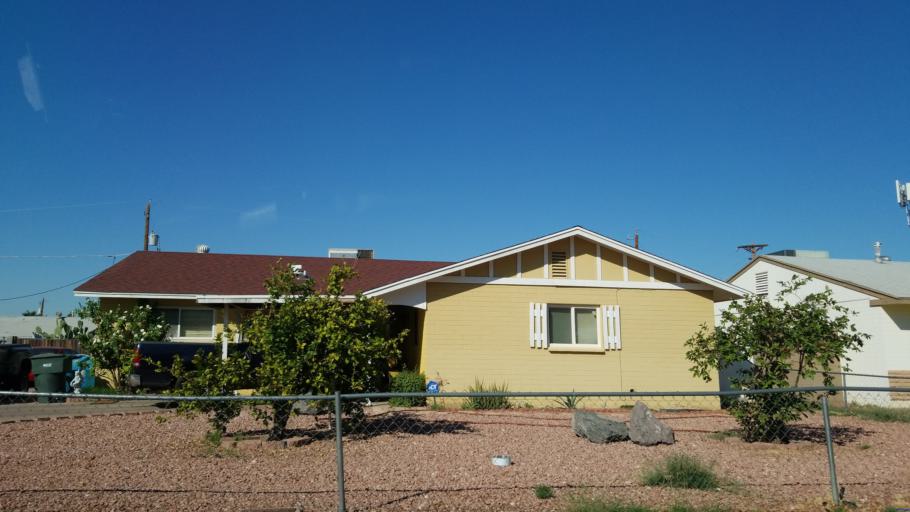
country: US
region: Arizona
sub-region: Maricopa County
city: Tolleson
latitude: 33.4927
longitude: -112.2297
